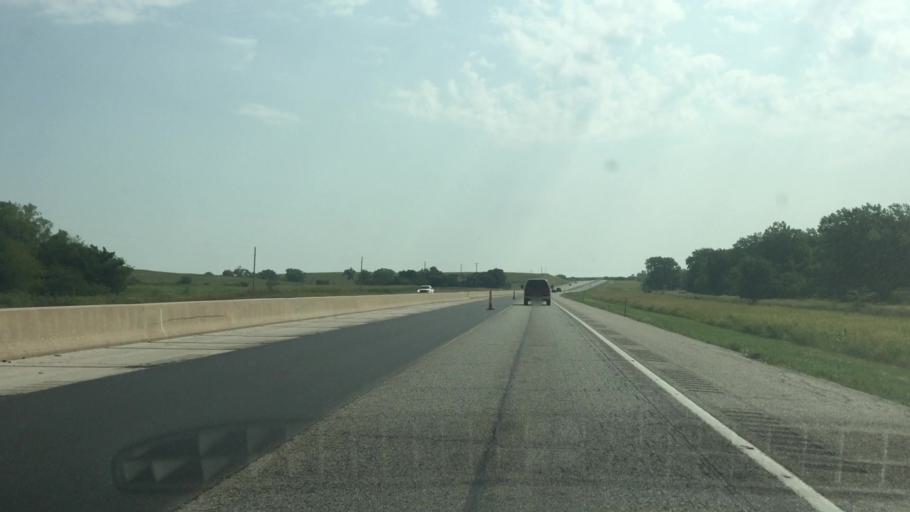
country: US
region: Kansas
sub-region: Chase County
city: Cottonwood Falls
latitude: 38.1470
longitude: -96.5065
